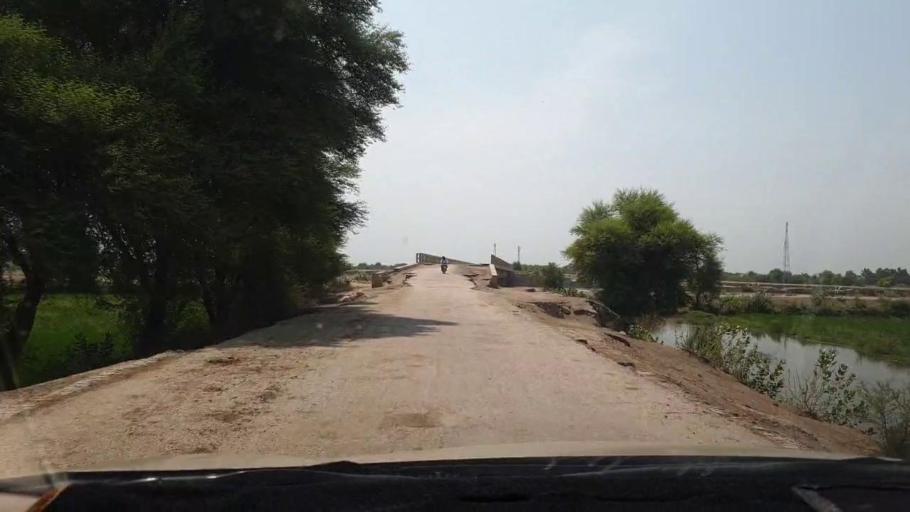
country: PK
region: Sindh
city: Larkana
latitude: 27.6251
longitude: 68.2741
